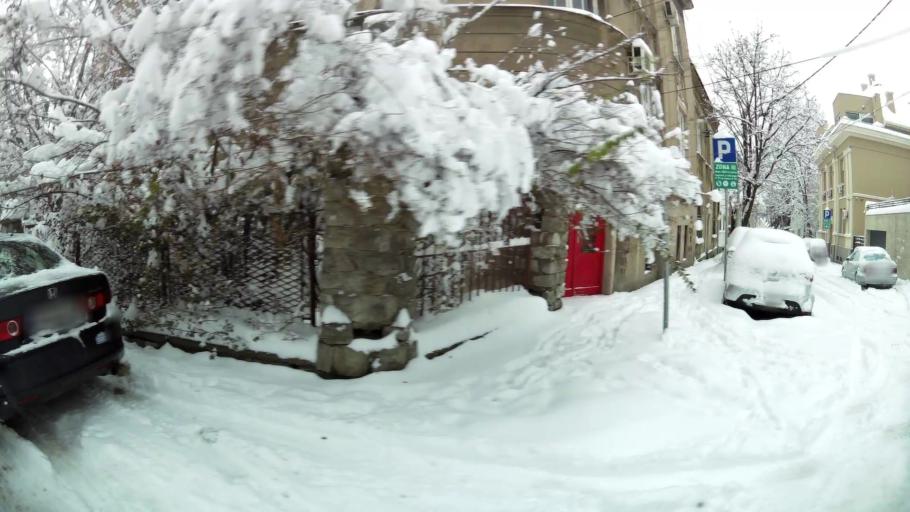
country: RS
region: Central Serbia
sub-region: Belgrade
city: Vracar
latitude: 44.7971
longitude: 20.4827
